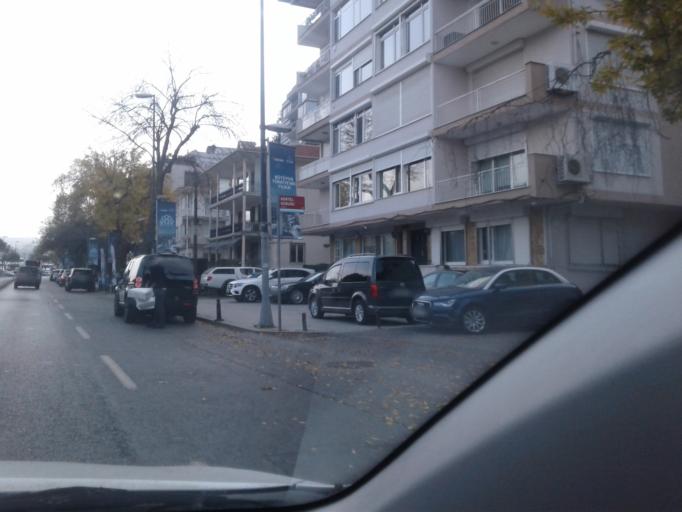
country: TR
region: Istanbul
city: UEskuedar
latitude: 41.0737
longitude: 29.0440
